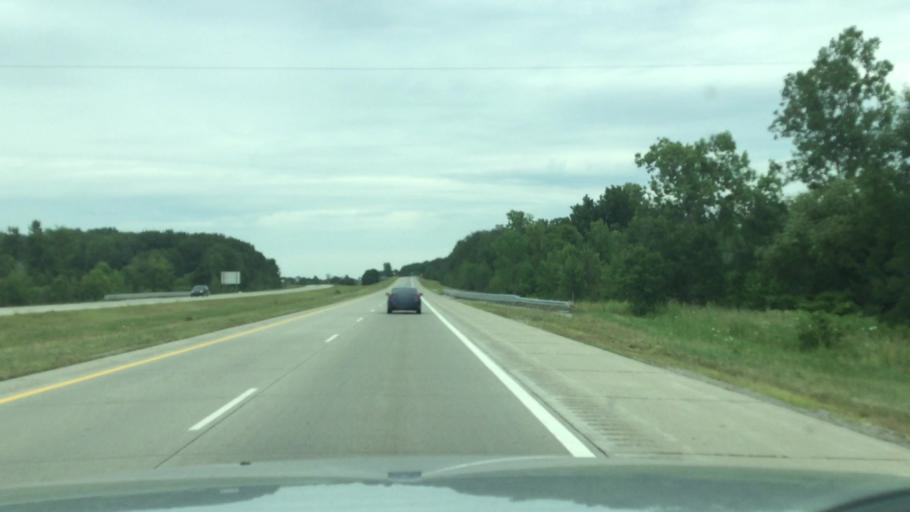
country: US
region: Michigan
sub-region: Genesee County
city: Grand Blanc
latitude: 42.9295
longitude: -83.6813
